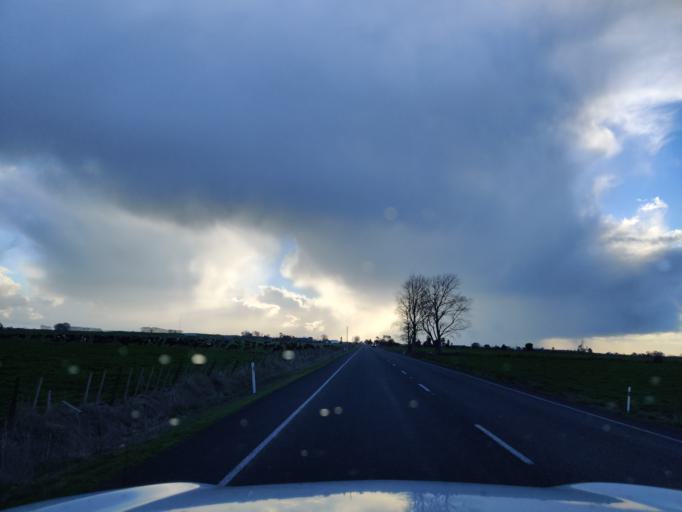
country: NZ
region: Waikato
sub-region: Hamilton City
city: Hamilton
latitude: -37.6943
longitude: 175.4347
